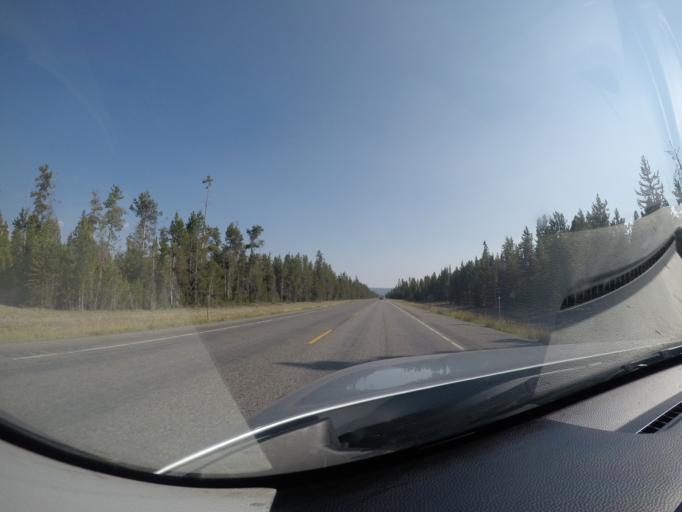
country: US
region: Montana
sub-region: Gallatin County
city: West Yellowstone
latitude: 44.6816
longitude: -111.1009
